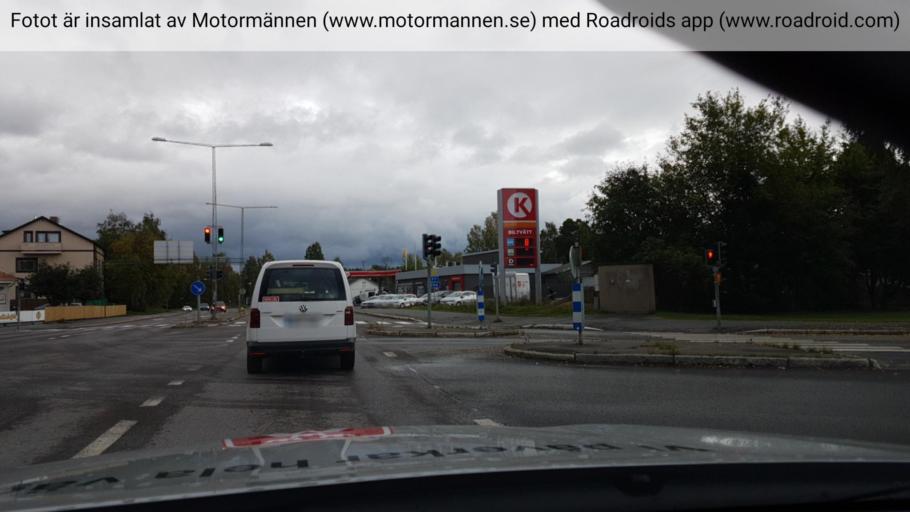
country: SE
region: Norrbotten
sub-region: Bodens Kommun
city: Boden
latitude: 65.8220
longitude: 21.6794
